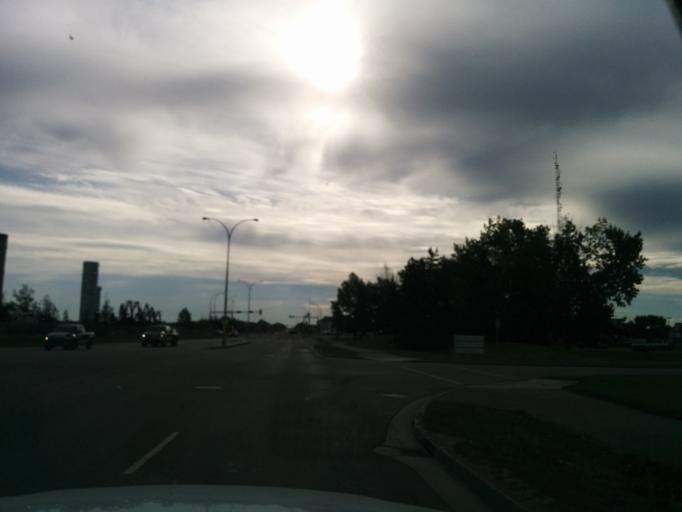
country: CA
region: Alberta
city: Grande Prairie
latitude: 55.1560
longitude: -118.8238
